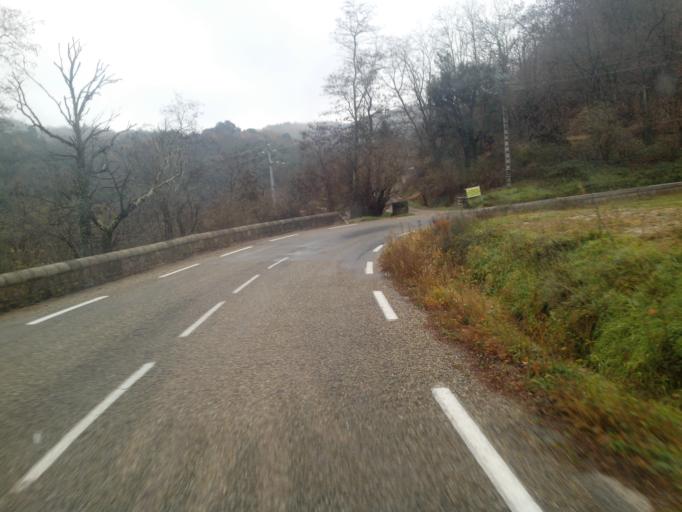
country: FR
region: Languedoc-Roussillon
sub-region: Departement du Gard
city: Lasalle
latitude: 44.0278
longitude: 3.8606
